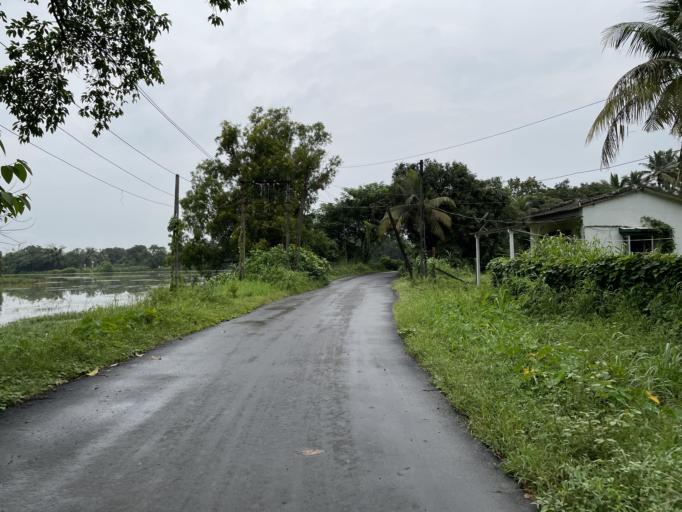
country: IN
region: Gujarat
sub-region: Valsad
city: Pardi
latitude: 20.4566
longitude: 72.9331
